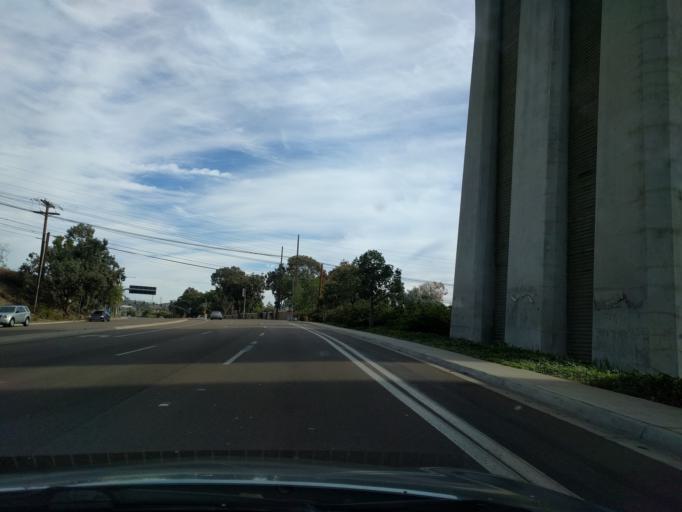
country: US
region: California
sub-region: San Diego County
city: San Diego
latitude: 32.7779
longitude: -117.1365
